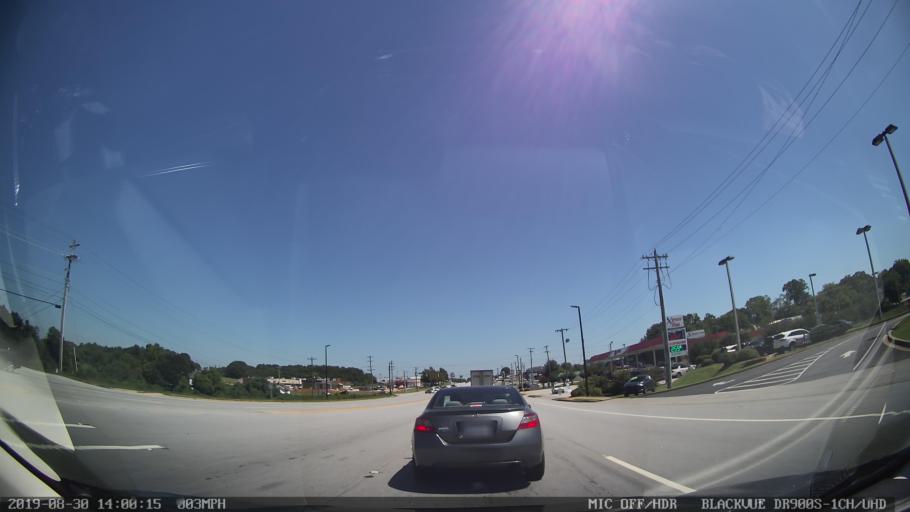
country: US
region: South Carolina
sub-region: Greenville County
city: Greer
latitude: 34.9495
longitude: -82.2170
